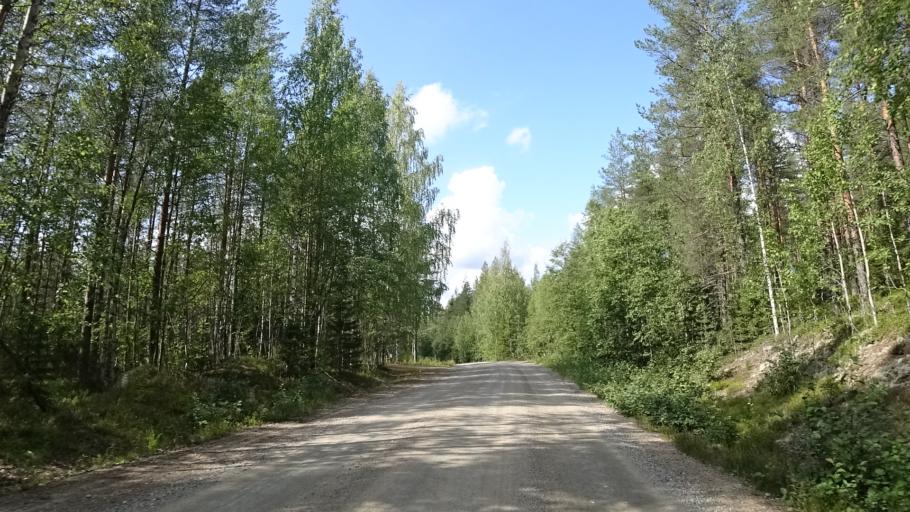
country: FI
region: North Karelia
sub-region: Joensuu
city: Ilomantsi
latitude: 62.9208
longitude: 31.3420
